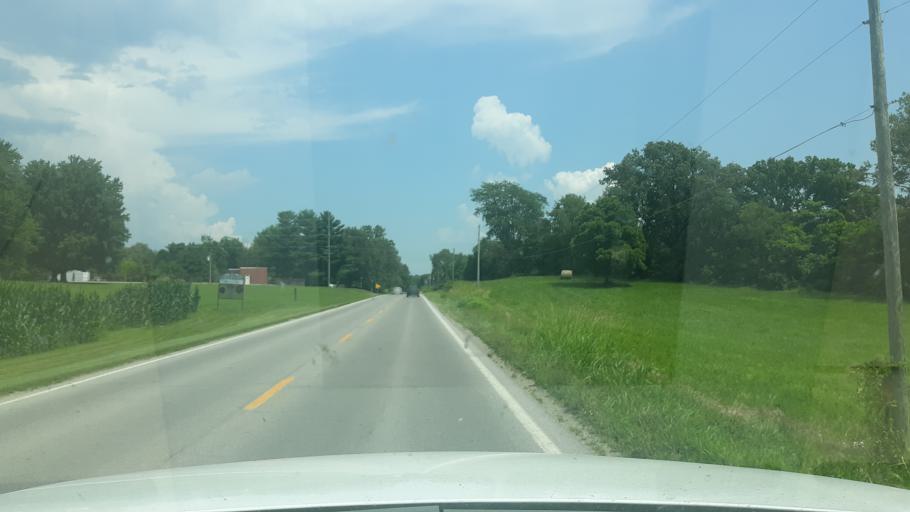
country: US
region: Illinois
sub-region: Saline County
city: Harrisburg
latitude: 37.8387
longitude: -88.5985
